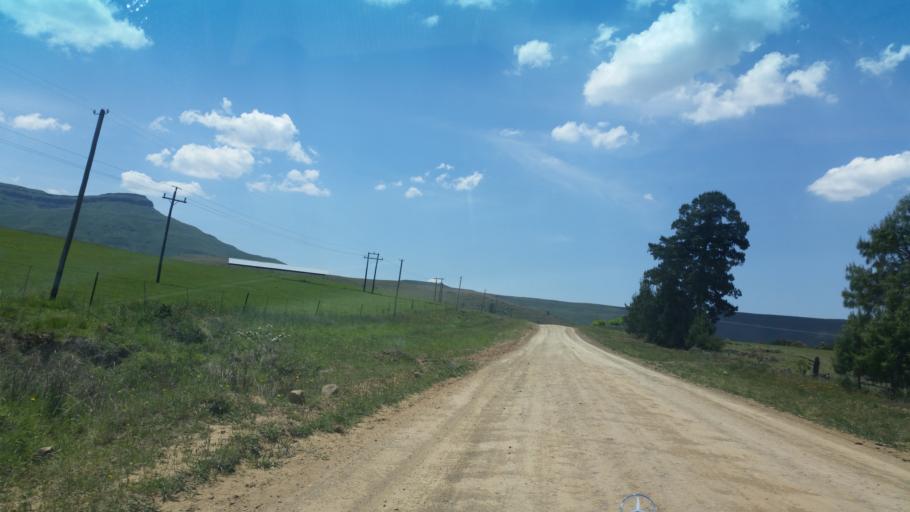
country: ZA
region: KwaZulu-Natal
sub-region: uMgungundlovu District Municipality
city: Impendle
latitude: -29.4623
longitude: 29.7394
